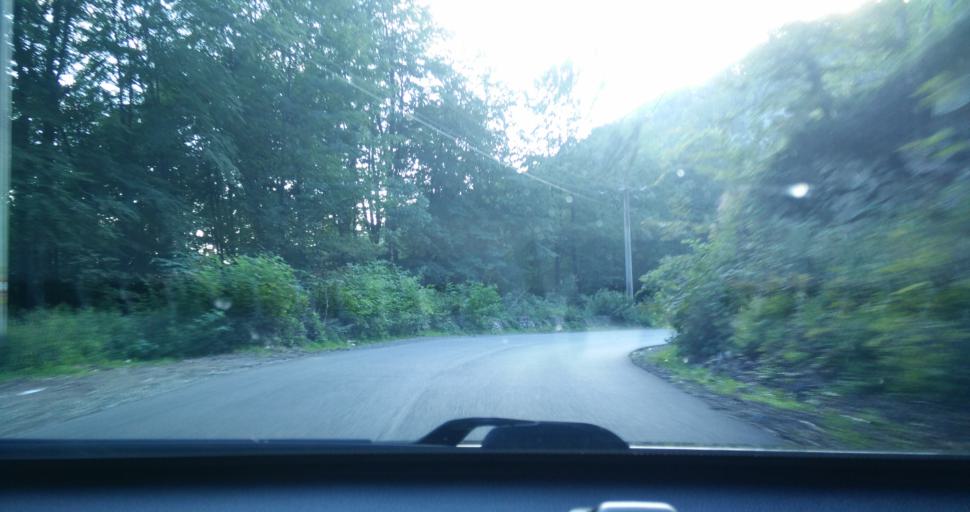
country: RO
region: Bihor
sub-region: Oras Nucet
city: Nucet
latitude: 46.5124
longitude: 22.6275
